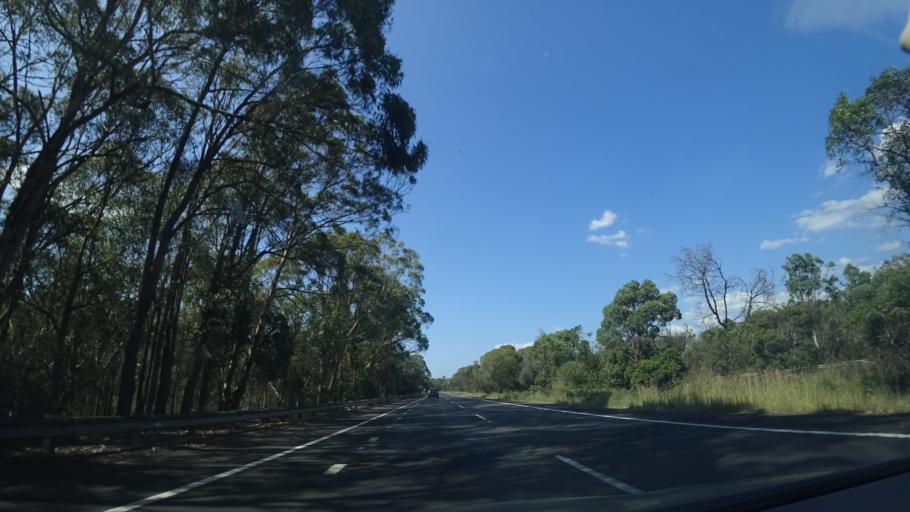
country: AU
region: New South Wales
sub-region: Wollondilly
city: Buxton
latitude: -34.3052
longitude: 150.6058
